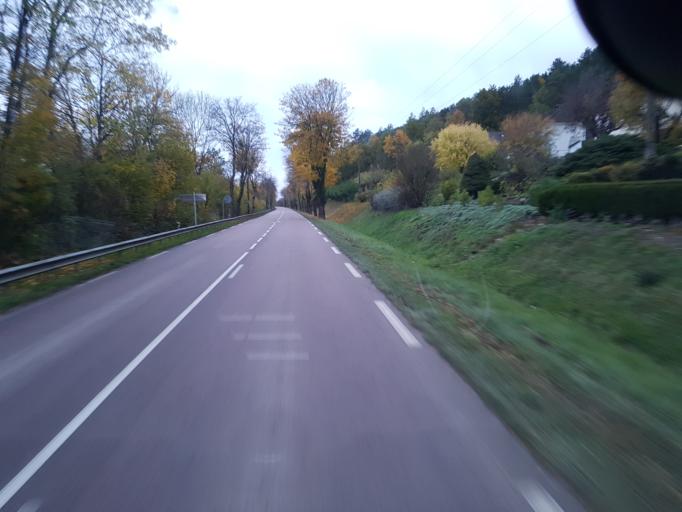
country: FR
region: Champagne-Ardenne
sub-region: Departement de l'Aube
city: Mussy-sur-Seine
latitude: 47.9975
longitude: 4.4812
